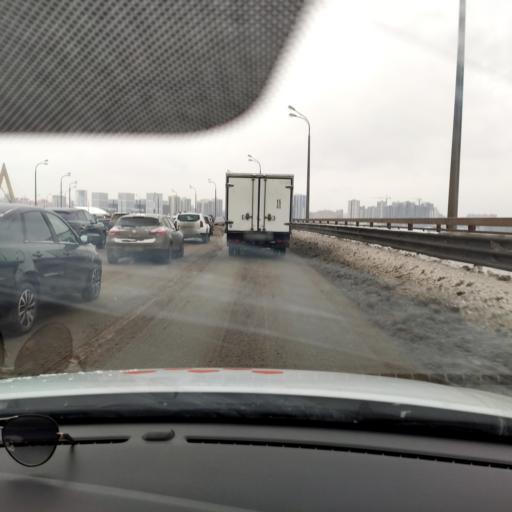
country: RU
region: Tatarstan
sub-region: Gorod Kazan'
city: Kazan
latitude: 55.8045
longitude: 49.1530
